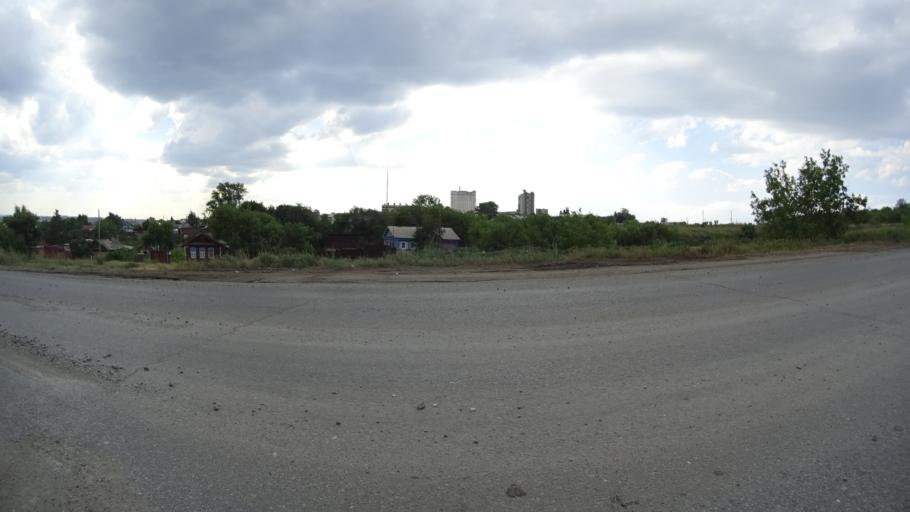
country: RU
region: Chelyabinsk
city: Troitsk
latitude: 54.1008
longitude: 61.5916
